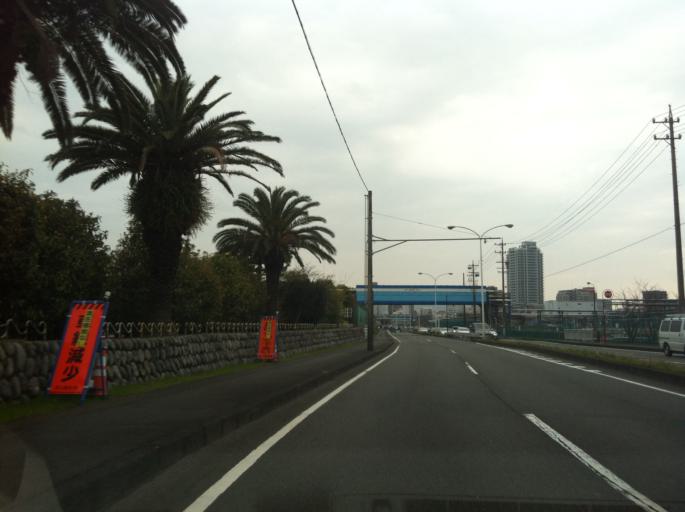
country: JP
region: Shizuoka
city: Shizuoka-shi
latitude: 35.0297
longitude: 138.4927
